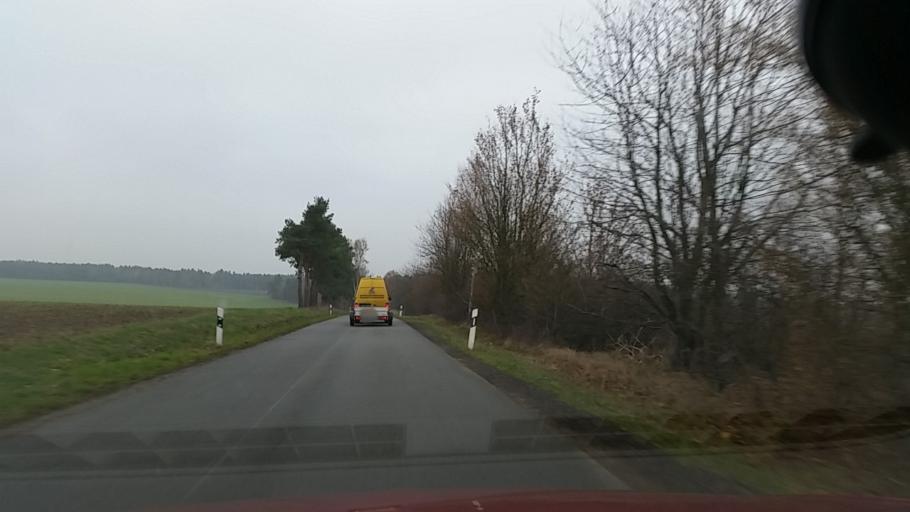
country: DE
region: Lower Saxony
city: Obernholz
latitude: 52.7727
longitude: 10.5864
